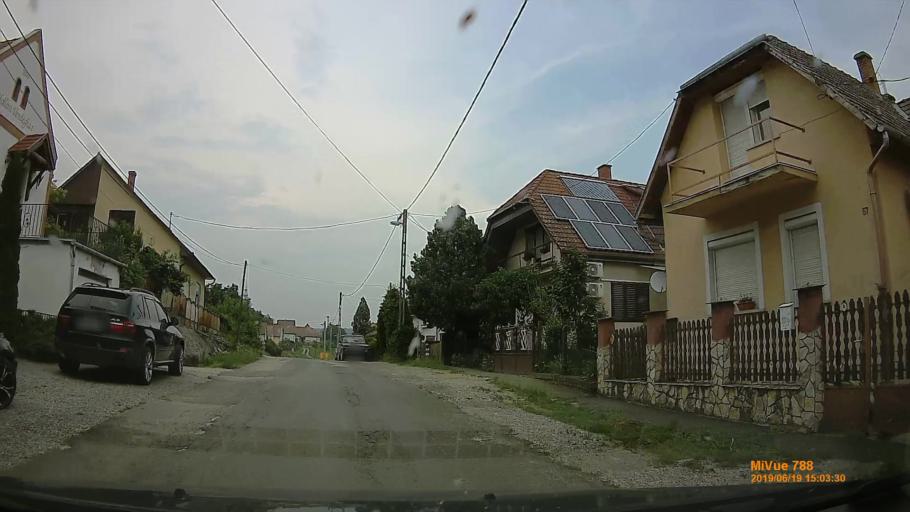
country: HU
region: Baranya
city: Szigetvar
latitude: 46.0947
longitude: 17.8062
